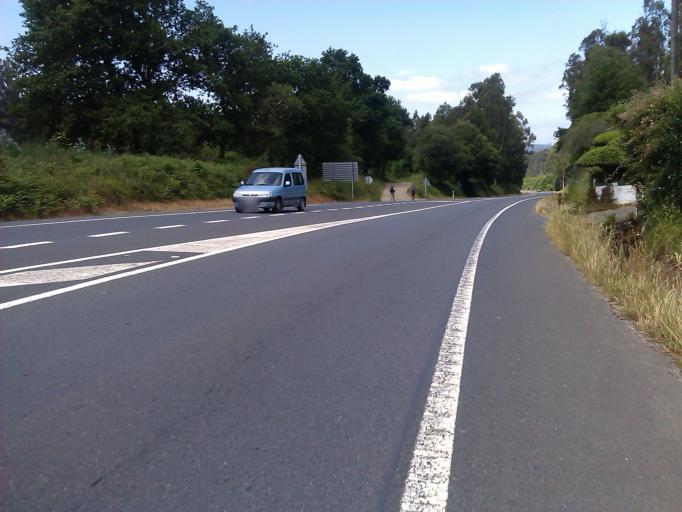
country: ES
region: Galicia
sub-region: Provincia da Coruna
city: Touro
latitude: 42.9157
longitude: -8.3246
